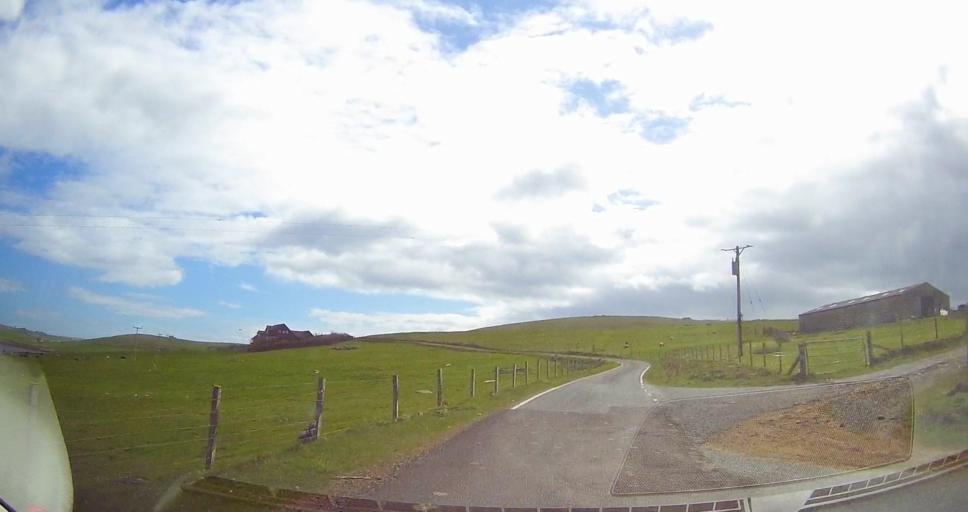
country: GB
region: Scotland
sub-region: Shetland Islands
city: Sandwick
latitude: 59.9335
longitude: -1.3456
